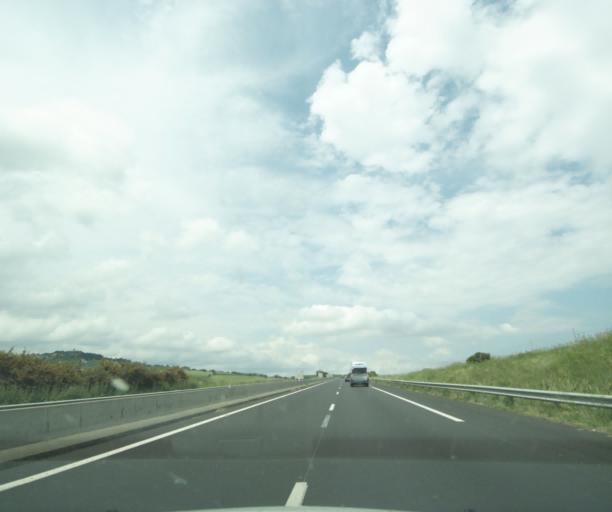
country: FR
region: Auvergne
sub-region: Departement du Puy-de-Dome
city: Tallende
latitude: 45.6730
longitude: 3.1425
